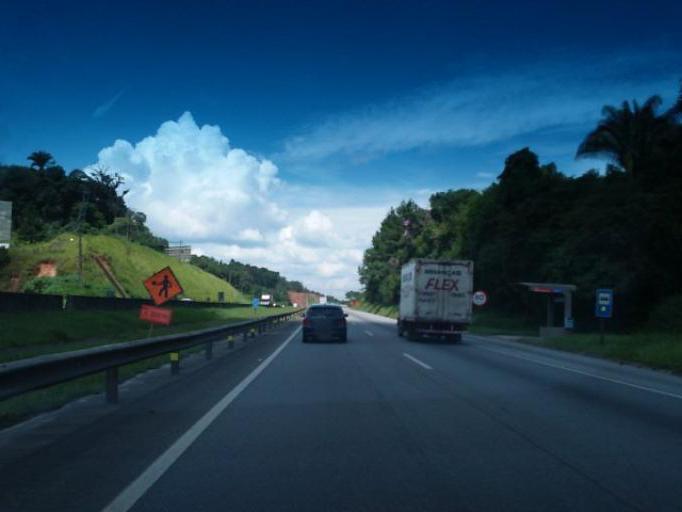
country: BR
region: Sao Paulo
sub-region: Juquitiba
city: Juquitiba
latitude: -23.9344
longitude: -47.0174
